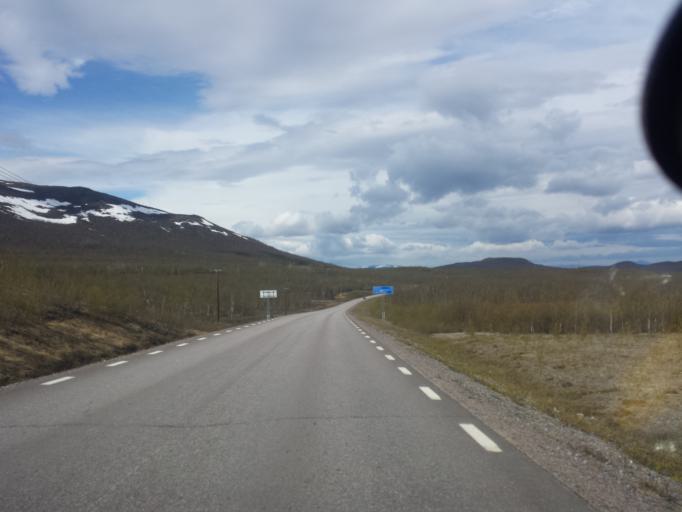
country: SE
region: Norrbotten
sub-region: Kiruna Kommun
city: Kiruna
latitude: 68.1593
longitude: 19.7782
